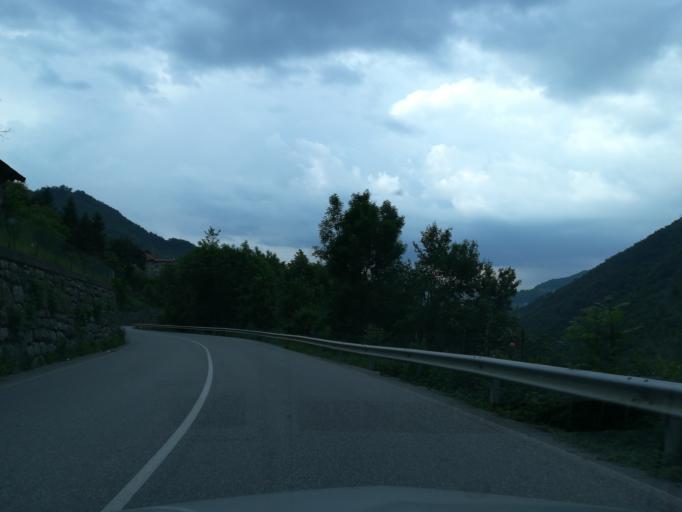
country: IT
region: Lombardy
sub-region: Provincia di Bergamo
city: Strozza
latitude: 45.7690
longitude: 9.5822
